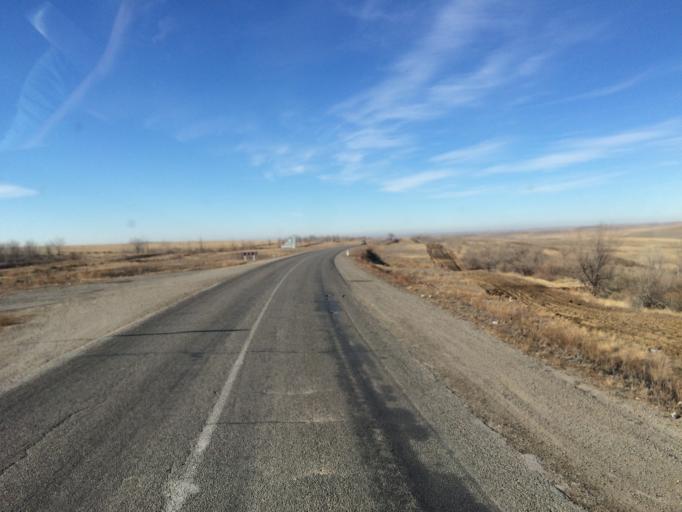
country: KZ
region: Aqtoebe
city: Aqtobe
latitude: 50.2818
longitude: 57.7487
